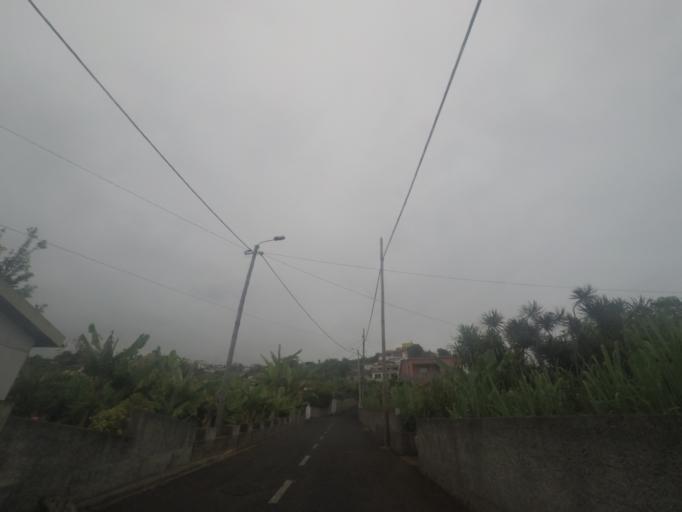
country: PT
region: Madeira
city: Camara de Lobos
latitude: 32.6511
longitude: -16.9545
